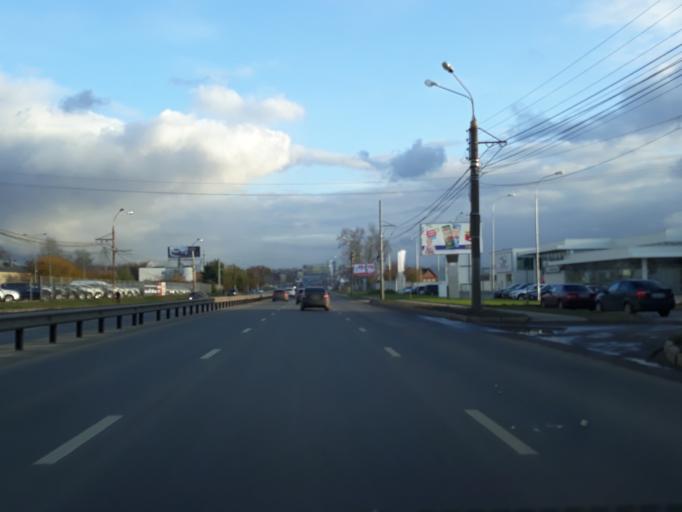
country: RU
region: Nizjnij Novgorod
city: Nizhniy Novgorod
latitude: 56.3007
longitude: 43.9227
